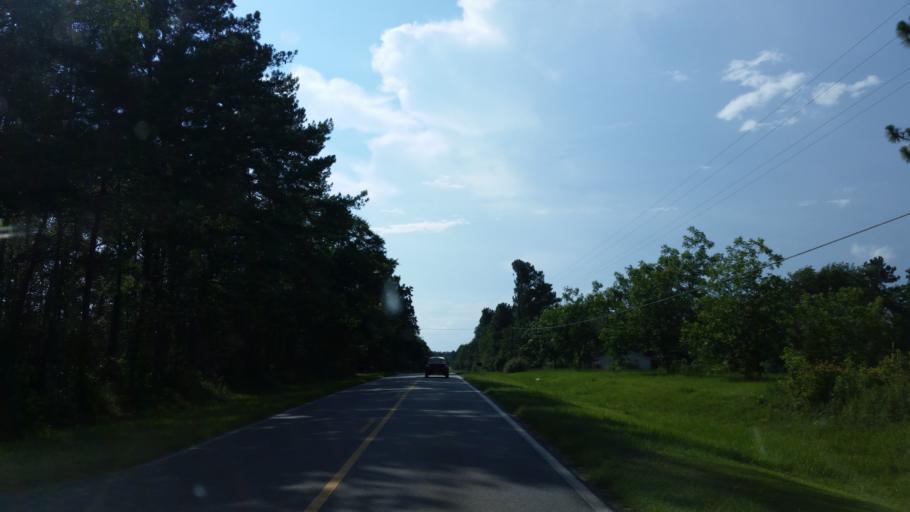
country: US
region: Georgia
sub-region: Lowndes County
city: Hahira
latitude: 30.9275
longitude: -83.3986
